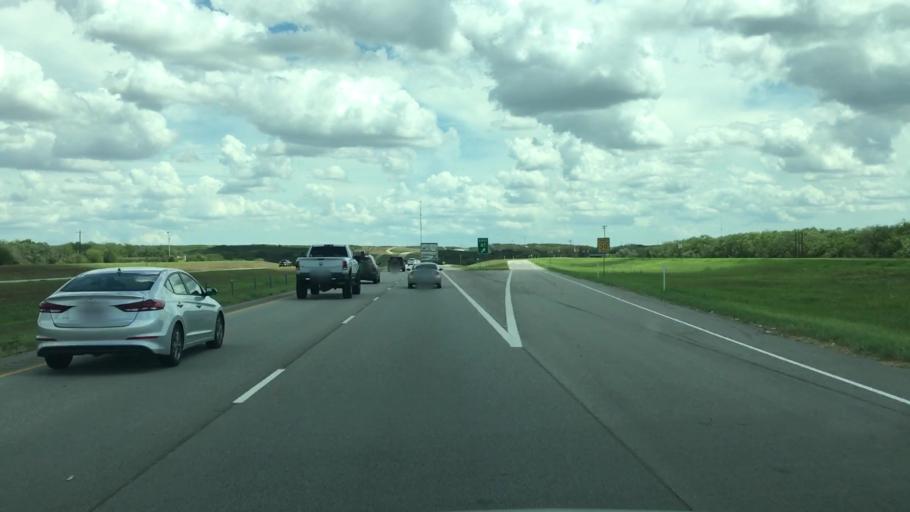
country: US
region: Texas
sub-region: Live Oak County
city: George West
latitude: 28.2658
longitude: -97.9379
